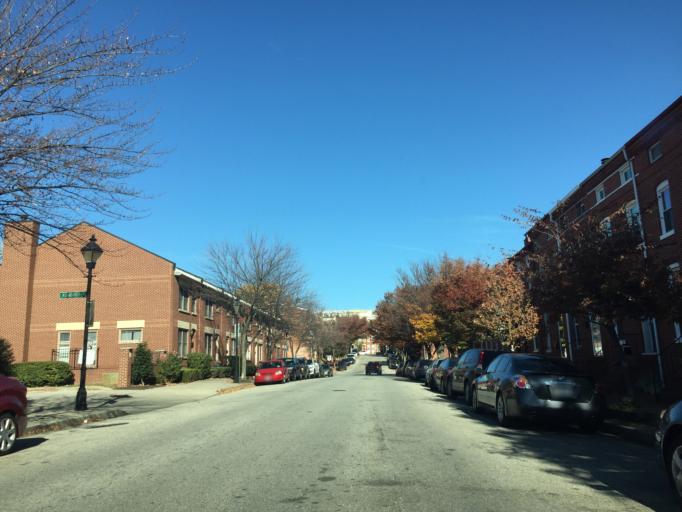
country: US
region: Maryland
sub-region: City of Baltimore
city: Baltimore
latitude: 39.2851
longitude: -76.6290
